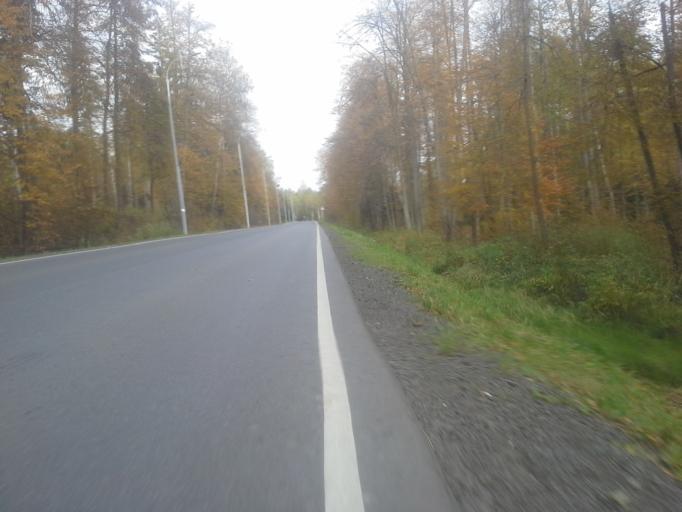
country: RU
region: Moskovskaya
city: Kievskij
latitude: 55.4099
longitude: 36.9387
